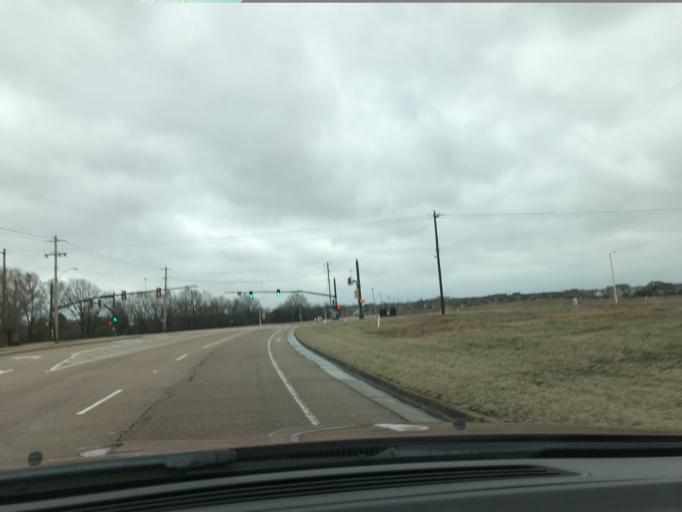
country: US
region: Tennessee
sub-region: Shelby County
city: Collierville
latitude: 35.0829
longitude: -89.6819
